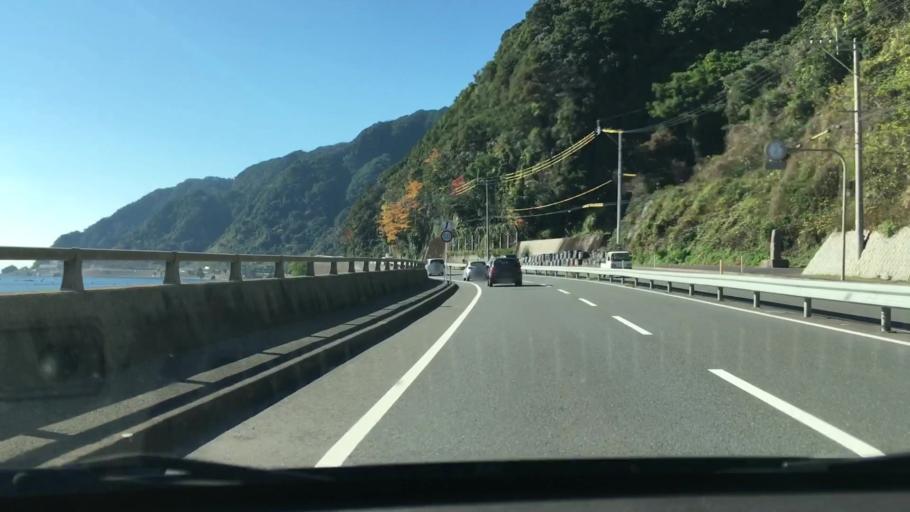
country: JP
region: Kagoshima
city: Kajiki
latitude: 31.6537
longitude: 130.6091
